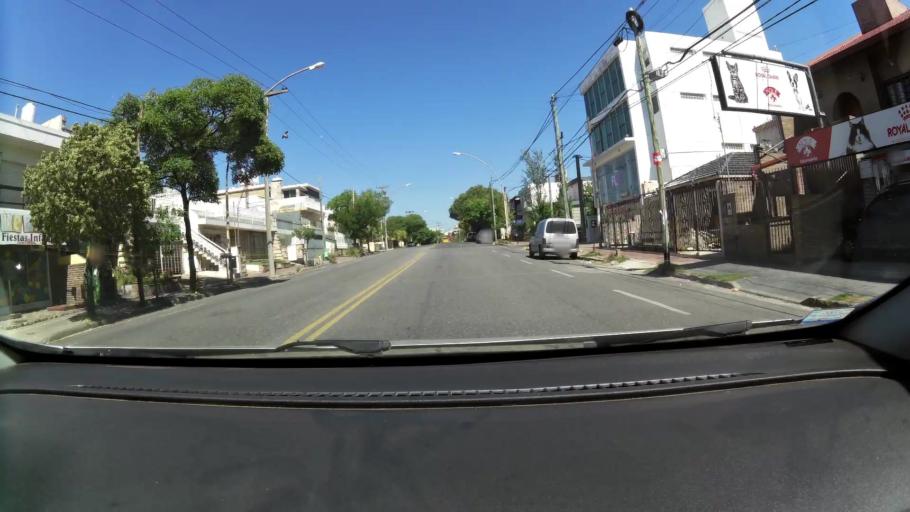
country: AR
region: Cordoba
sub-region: Departamento de Capital
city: Cordoba
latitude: -31.4167
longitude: -64.2024
